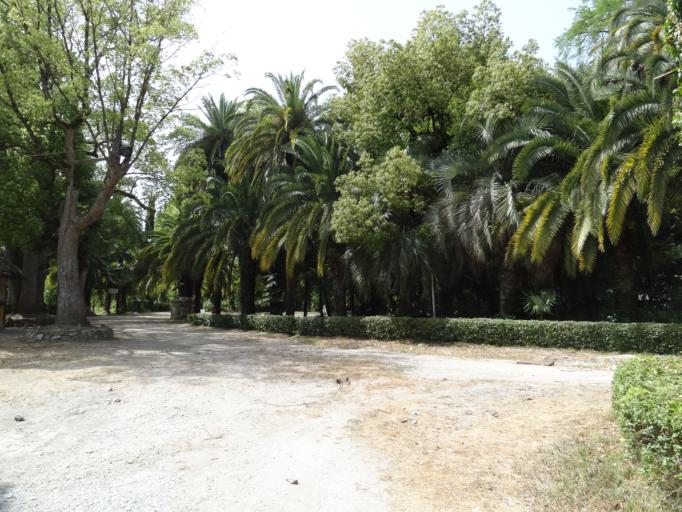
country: GE
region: Abkhazia
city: Gagra
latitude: 43.3233
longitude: 40.2301
